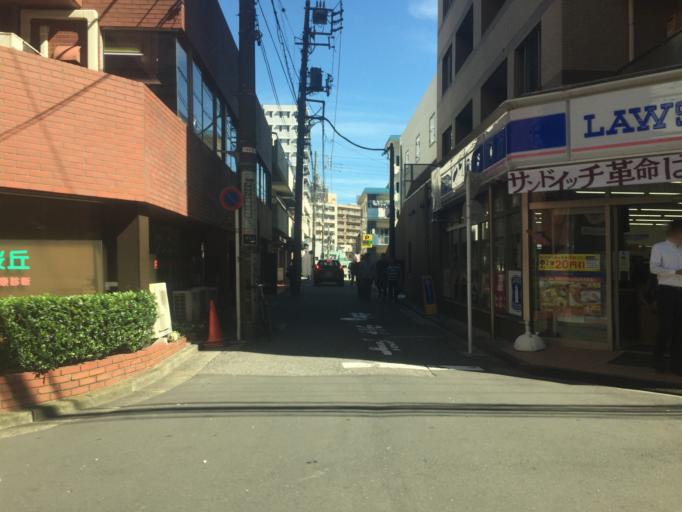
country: JP
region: Tokyo
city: Tokyo
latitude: 35.6553
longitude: 139.7012
